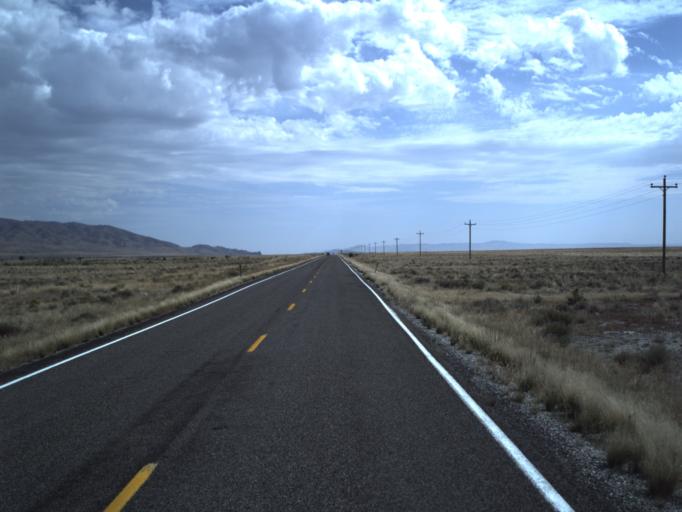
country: US
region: Utah
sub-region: Tooele County
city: Wendover
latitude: 41.4290
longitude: -113.8183
